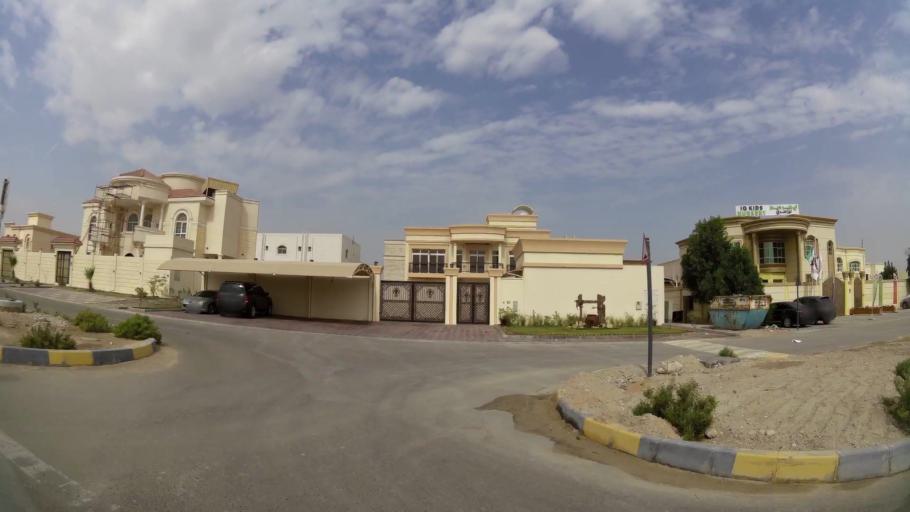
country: AE
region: Abu Dhabi
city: Abu Dhabi
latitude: 24.3095
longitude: 54.6493
